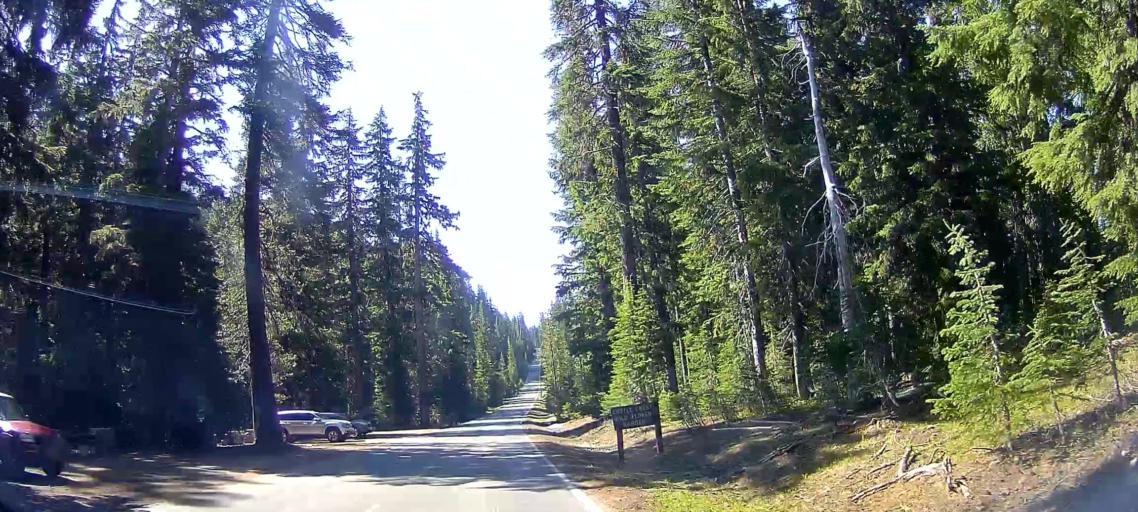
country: US
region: Oregon
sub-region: Jackson County
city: Shady Cove
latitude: 42.8911
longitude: -122.1325
